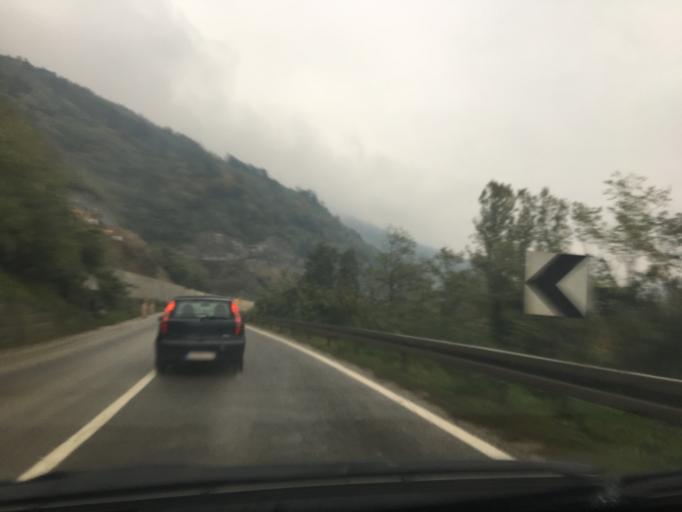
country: RS
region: Central Serbia
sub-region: Pcinjski Okrug
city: Vladicin Han
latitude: 42.7663
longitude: 22.0852
